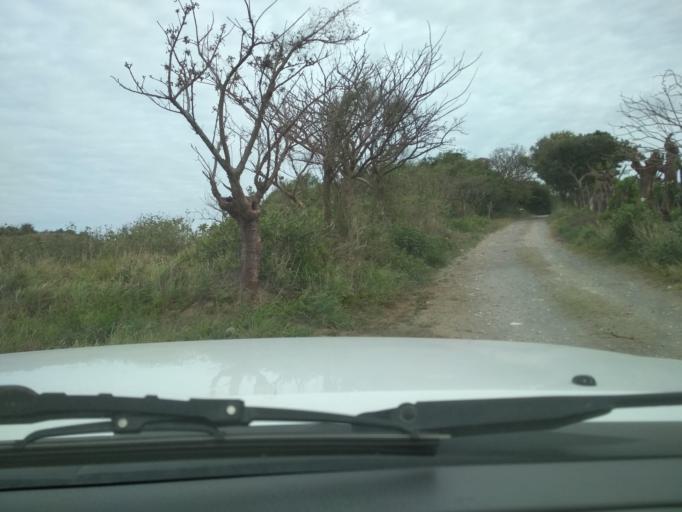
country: MX
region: Veracruz
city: Anton Lizardo
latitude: 19.0514
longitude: -95.9897
